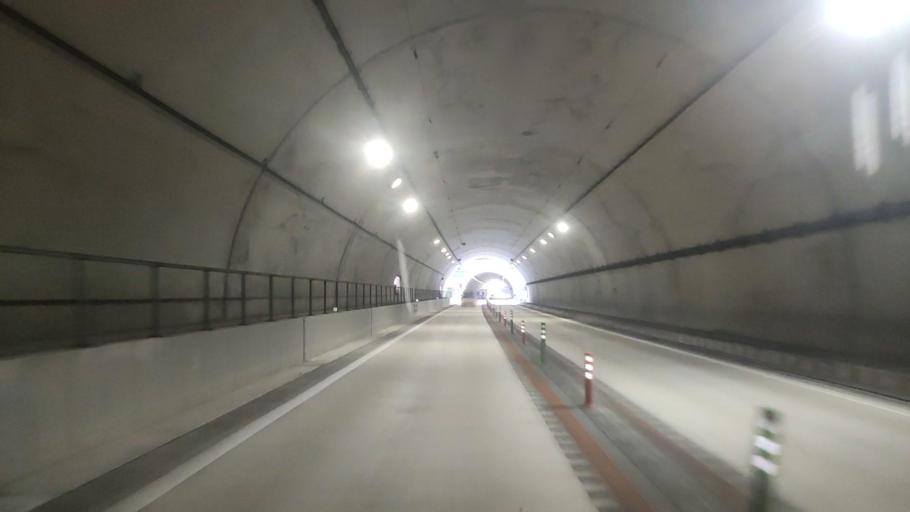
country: JP
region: Wakayama
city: Tanabe
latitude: 33.5960
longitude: 135.4349
